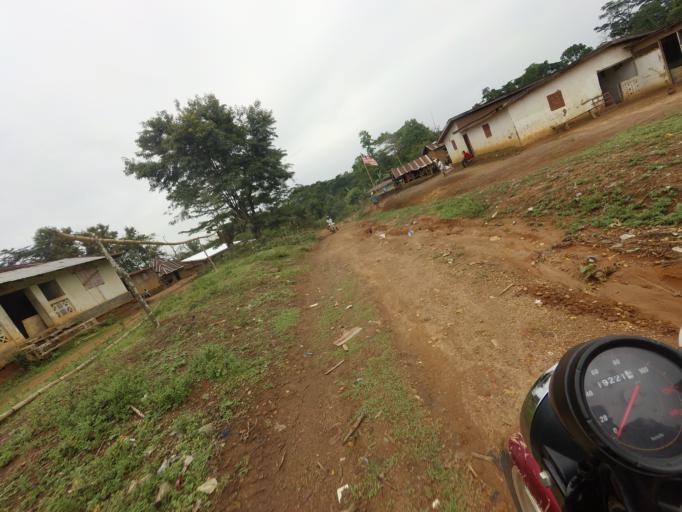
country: LR
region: Nimba
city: New Yekepa
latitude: 7.6536
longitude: -8.5566
